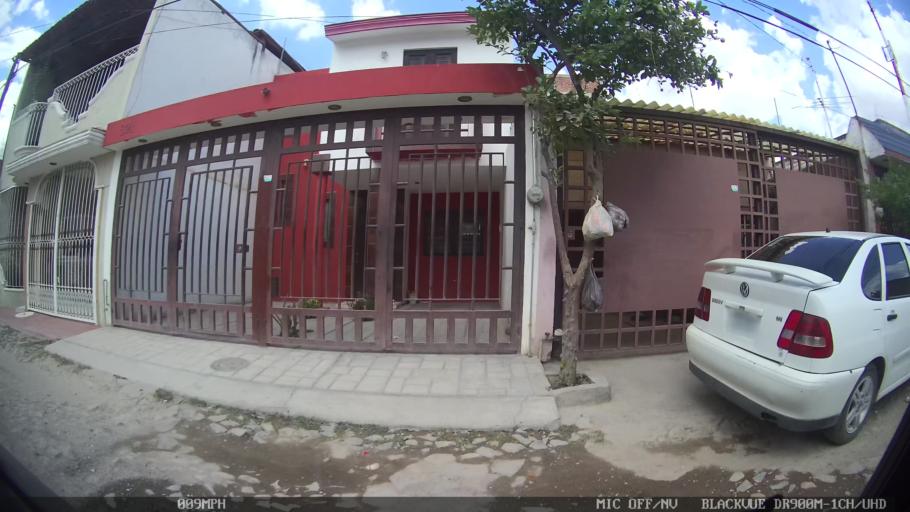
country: MX
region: Jalisco
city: Tlaquepaque
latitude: 20.6764
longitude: -103.2582
